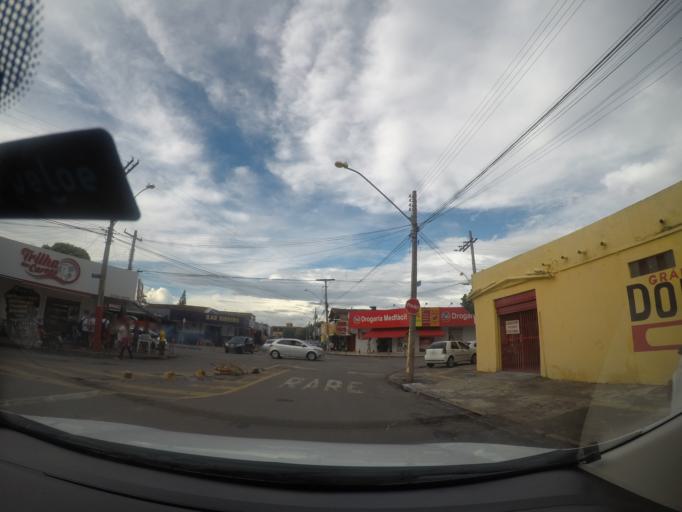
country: BR
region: Goias
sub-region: Goiania
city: Goiania
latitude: -16.6686
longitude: -49.2806
